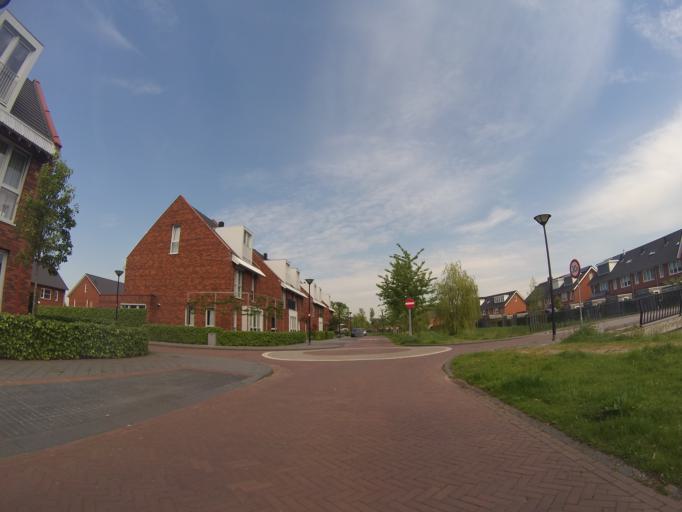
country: NL
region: Gelderland
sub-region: Gemeente Ede
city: Ederveen
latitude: 52.0755
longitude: 5.5496
